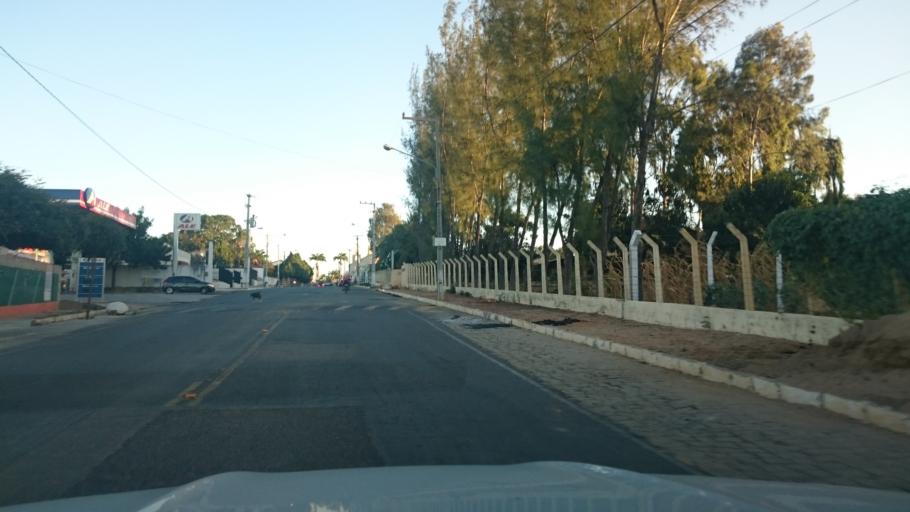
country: BR
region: Rio Grande do Norte
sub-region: Umarizal
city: Umarizal
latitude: -6.0215
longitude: -37.9868
